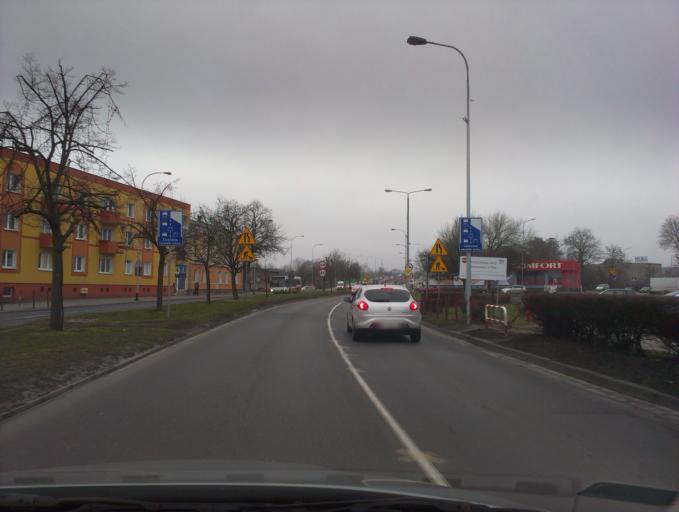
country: PL
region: Greater Poland Voivodeship
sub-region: Powiat pilski
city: Pila
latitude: 53.1464
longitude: 16.7389
